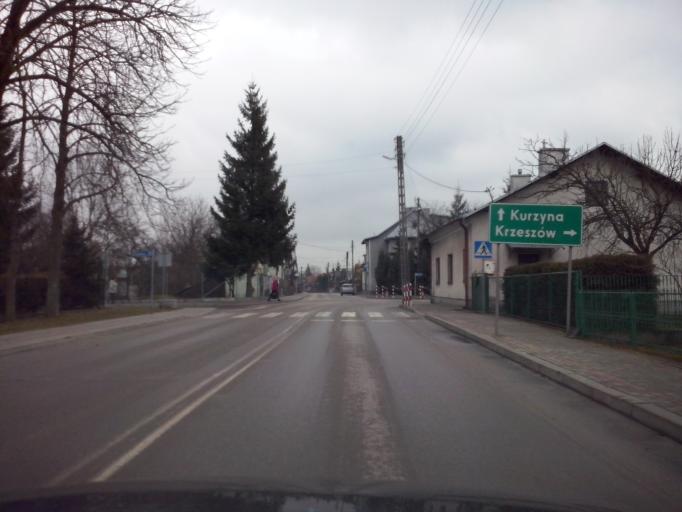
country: PL
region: Subcarpathian Voivodeship
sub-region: Powiat nizanski
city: Ulanow
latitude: 50.4894
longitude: 22.2645
